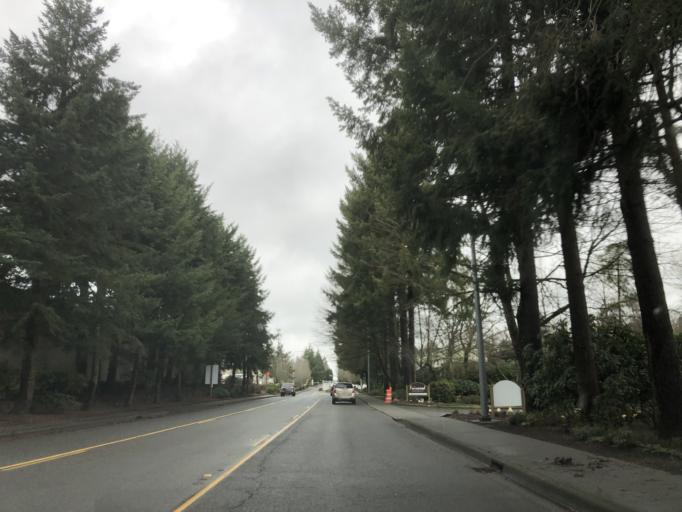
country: US
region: Washington
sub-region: King County
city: Fairwood
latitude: 47.4457
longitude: -122.1487
